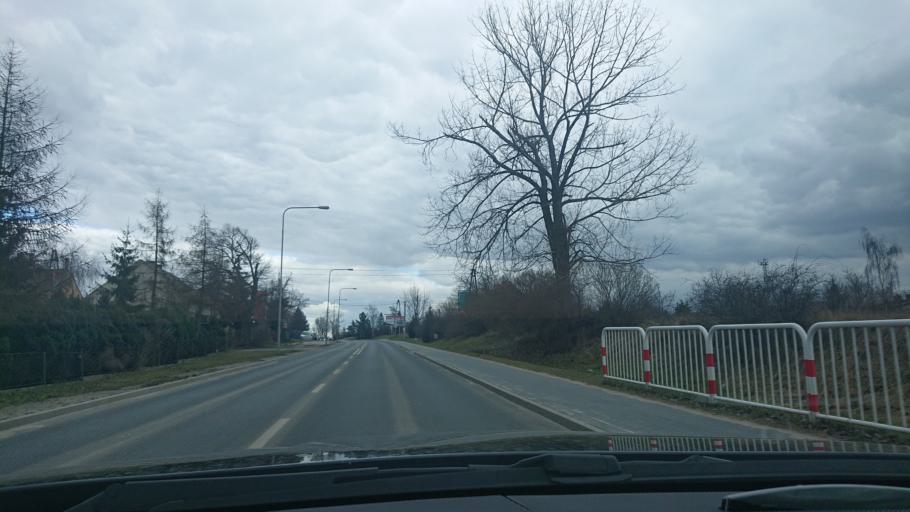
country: PL
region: Greater Poland Voivodeship
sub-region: Powiat gnieznienski
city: Gniezno
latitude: 52.5411
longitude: 17.6386
